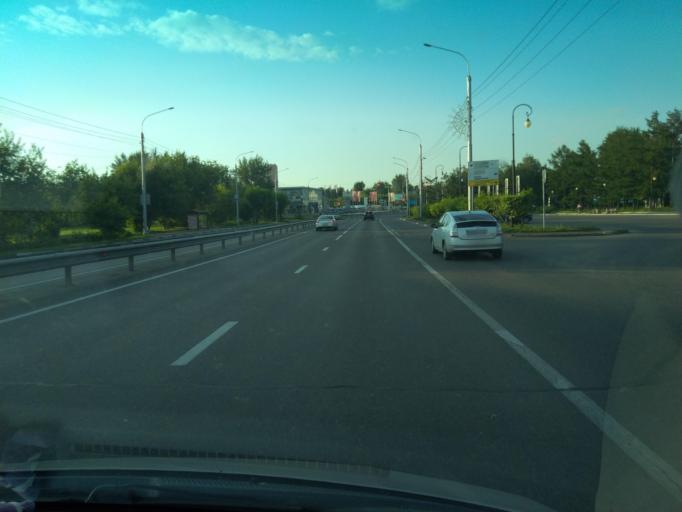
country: RU
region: Krasnoyarskiy
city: Krasnoyarsk
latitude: 56.0224
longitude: 92.8853
